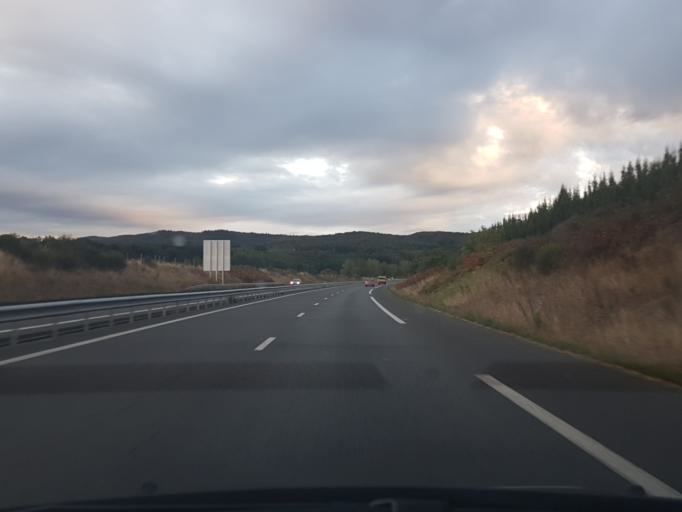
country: FR
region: Midi-Pyrenees
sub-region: Departement de l'Ariege
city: Verniolle
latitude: 43.0577
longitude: 1.6486
